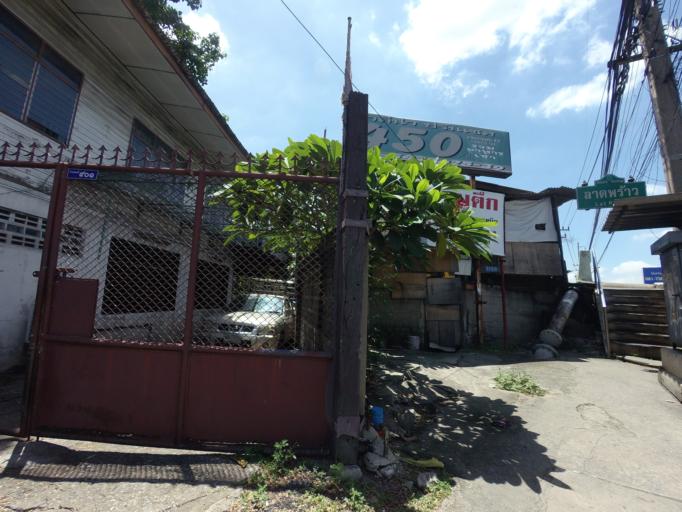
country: TH
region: Bangkok
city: Lat Phrao
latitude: 13.7977
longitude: 100.5888
